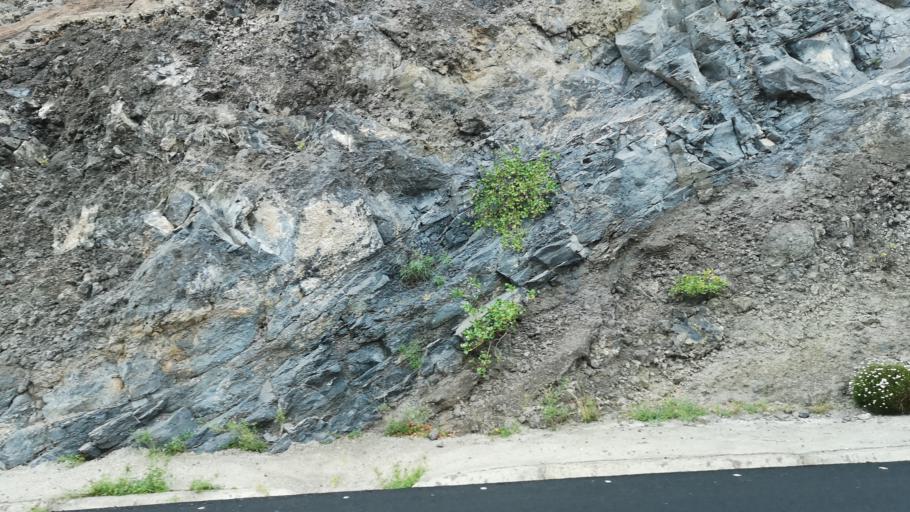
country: ES
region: Canary Islands
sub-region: Provincia de Santa Cruz de Tenerife
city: Alajero
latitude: 28.0548
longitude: -17.2008
